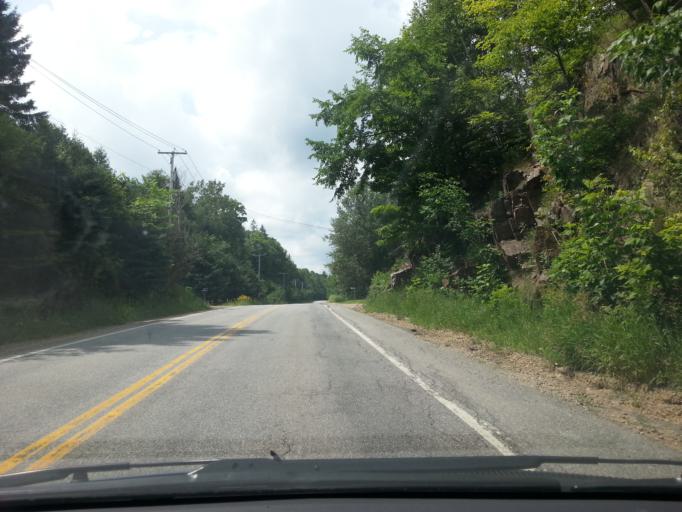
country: CA
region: Quebec
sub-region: Outaouais
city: Val-des-Monts
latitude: 45.6580
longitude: -75.7433
